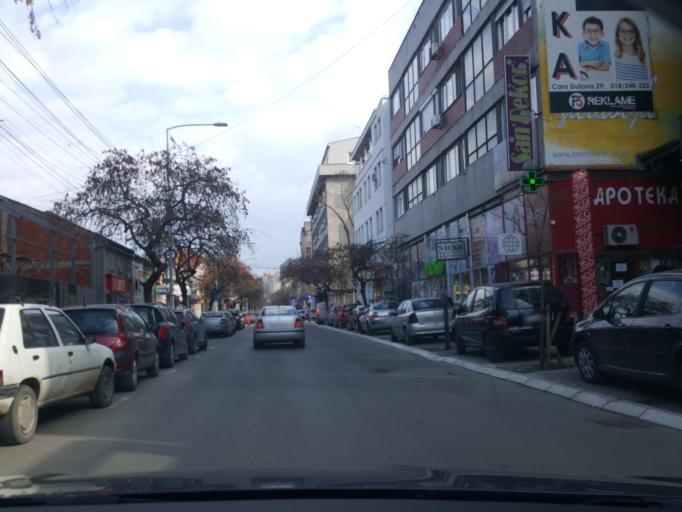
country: RS
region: Central Serbia
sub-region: Nisavski Okrug
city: Nis
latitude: 43.3169
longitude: 21.8949
